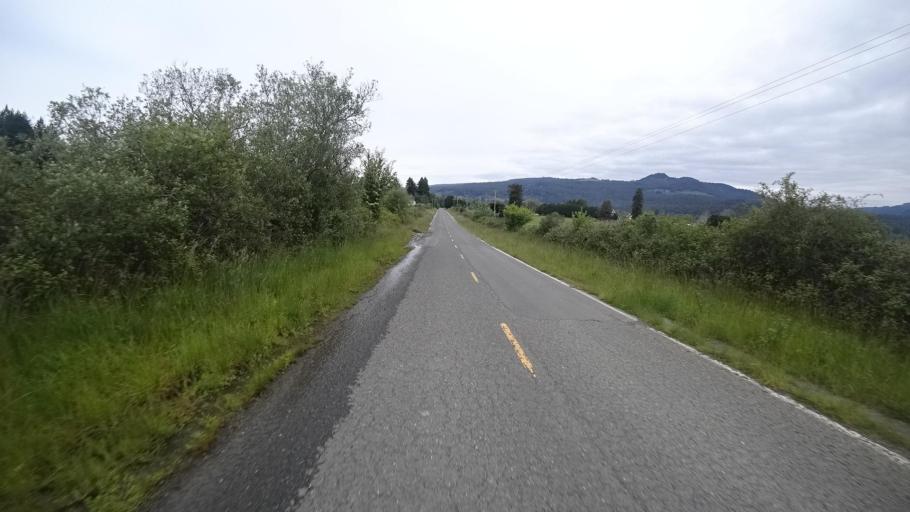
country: US
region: California
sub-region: Humboldt County
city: Blue Lake
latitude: 40.8599
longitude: -123.9957
